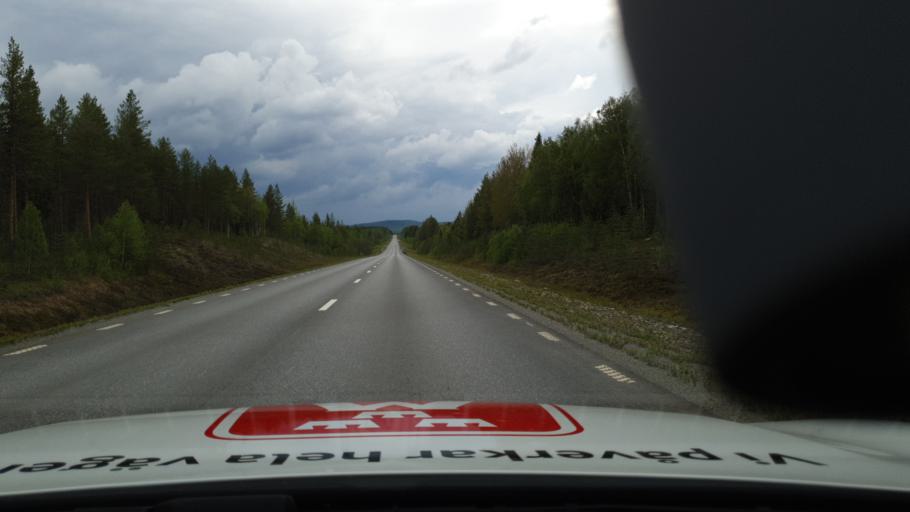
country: SE
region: Vaesterbotten
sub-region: Dorotea Kommun
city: Dorotea
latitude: 64.2707
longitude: 16.5000
